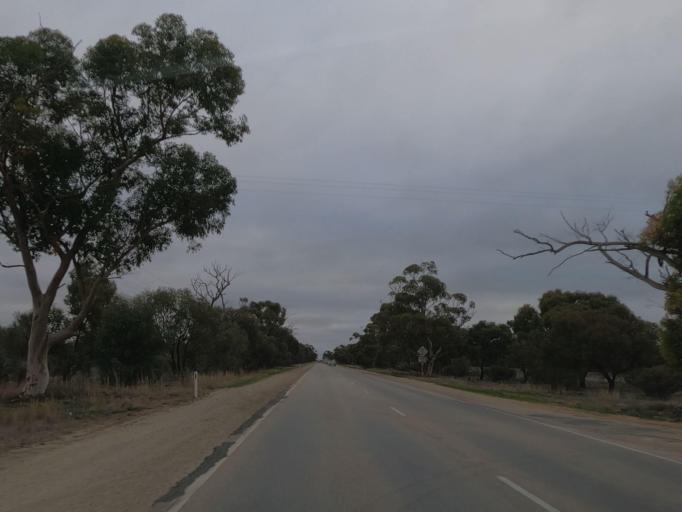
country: AU
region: Victoria
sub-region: Swan Hill
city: Swan Hill
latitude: -35.4046
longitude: 143.5803
